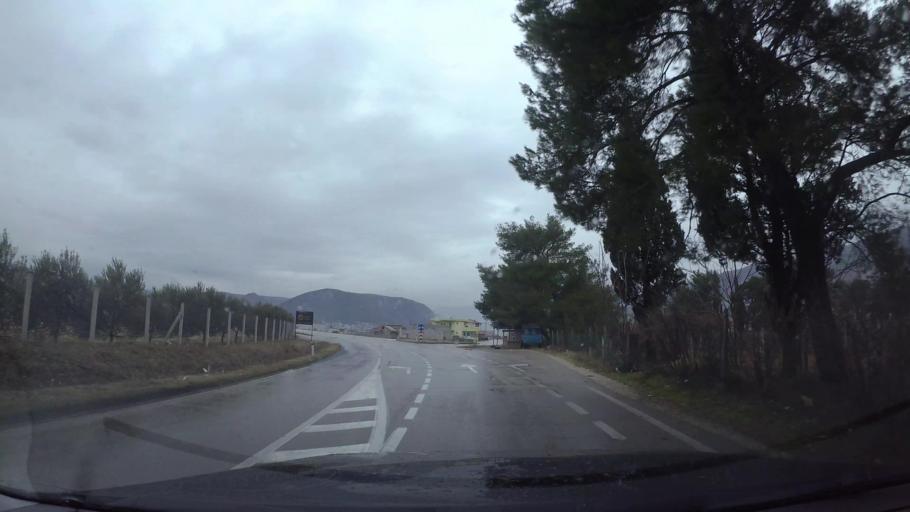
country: BA
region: Federation of Bosnia and Herzegovina
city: Rodoc
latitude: 43.3008
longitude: 17.8404
